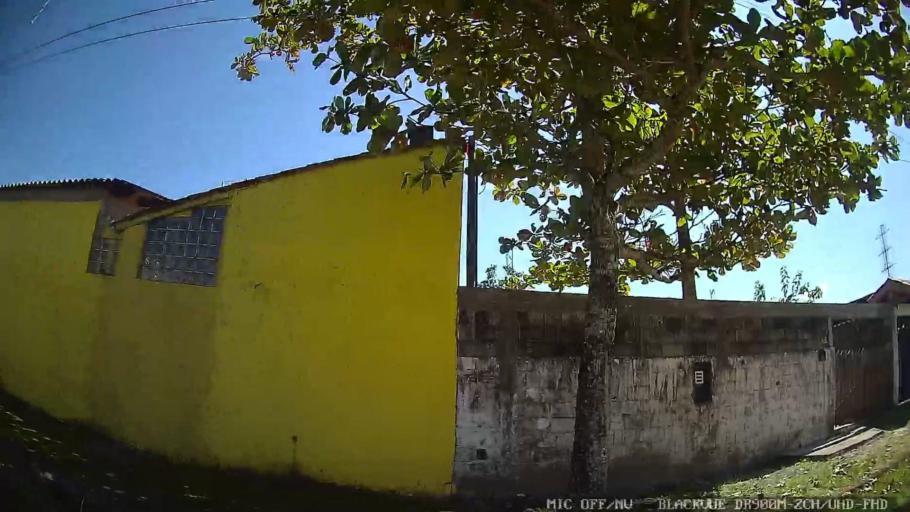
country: BR
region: Sao Paulo
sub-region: Itanhaem
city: Itanhaem
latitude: -24.2073
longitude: -46.8552
